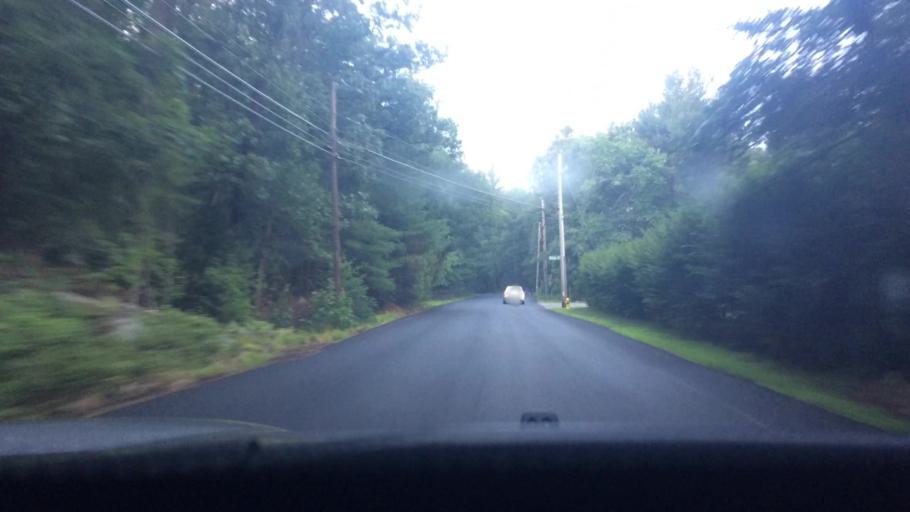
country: US
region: Massachusetts
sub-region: Middlesex County
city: North Reading
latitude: 42.6152
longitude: -71.0926
